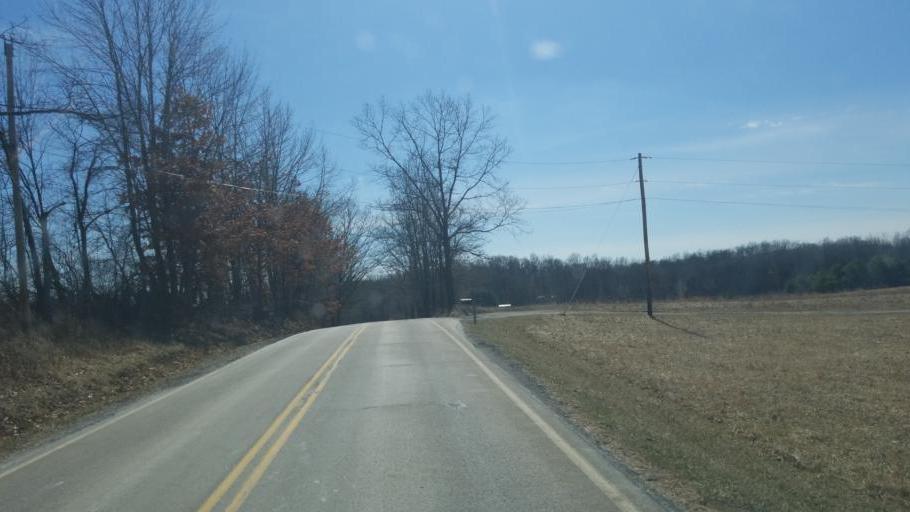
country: US
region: Ohio
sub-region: Knox County
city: Oak Hill
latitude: 40.4576
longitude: -82.1303
